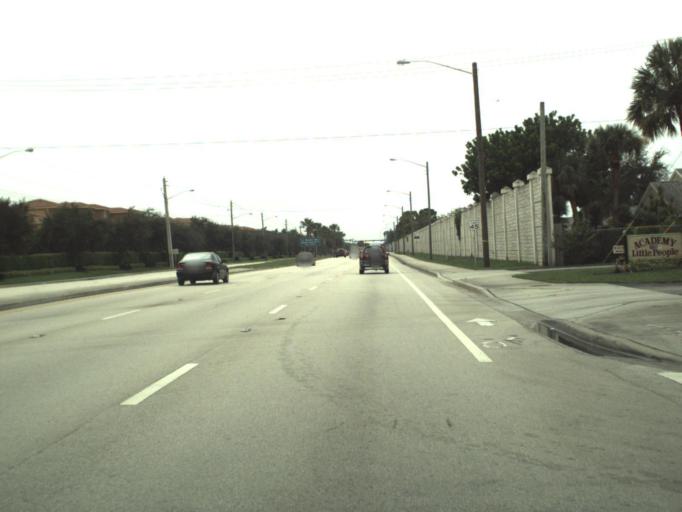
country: US
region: Florida
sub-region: Palm Beach County
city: Schall Circle
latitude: 26.7455
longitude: -80.1096
